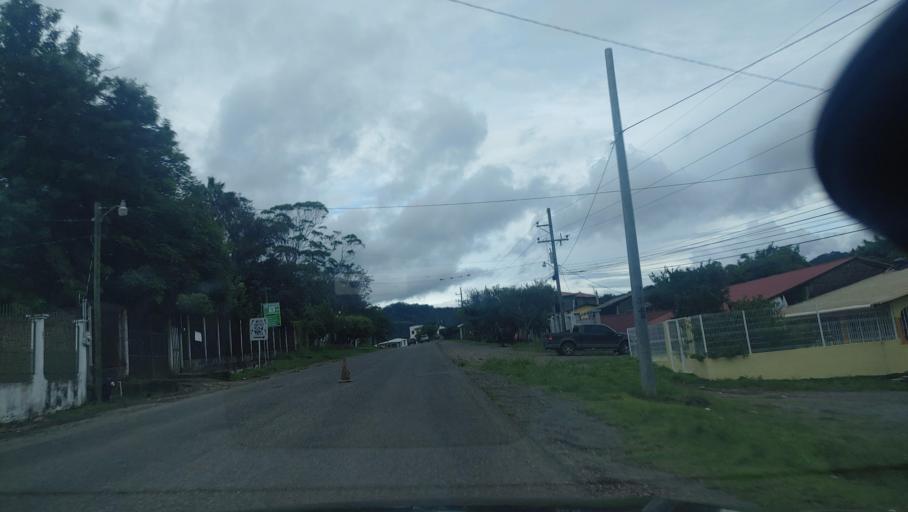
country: HN
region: Choluteca
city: San Marcos de Colon
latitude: 13.3770
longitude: -86.9036
